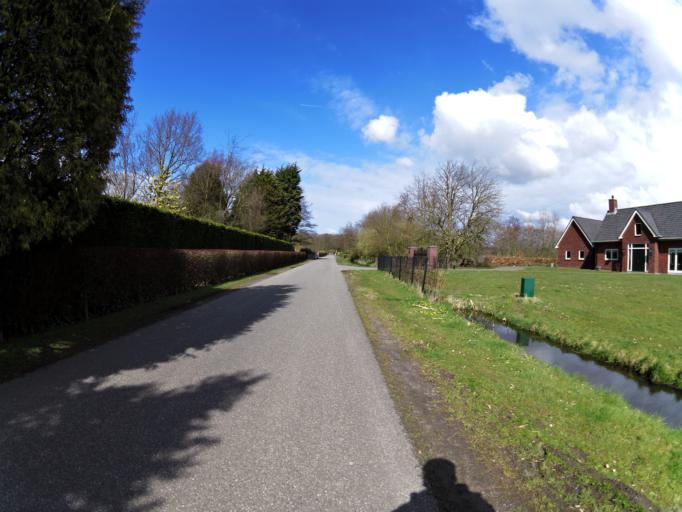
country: NL
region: South Holland
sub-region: Gemeente Hellevoetsluis
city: Nieuw-Helvoet
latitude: 51.8922
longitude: 4.0752
